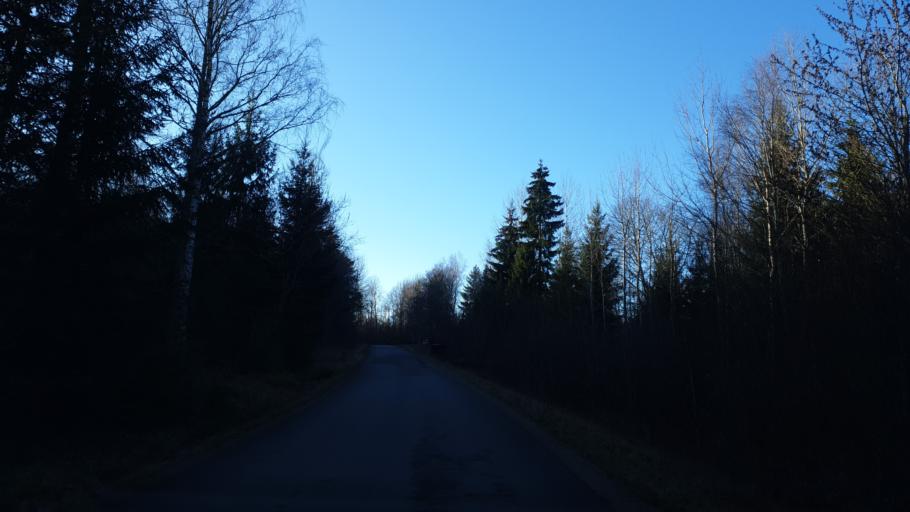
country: SE
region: Blekinge
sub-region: Karlskrona Kommun
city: Nattraby
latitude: 56.2694
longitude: 15.4523
